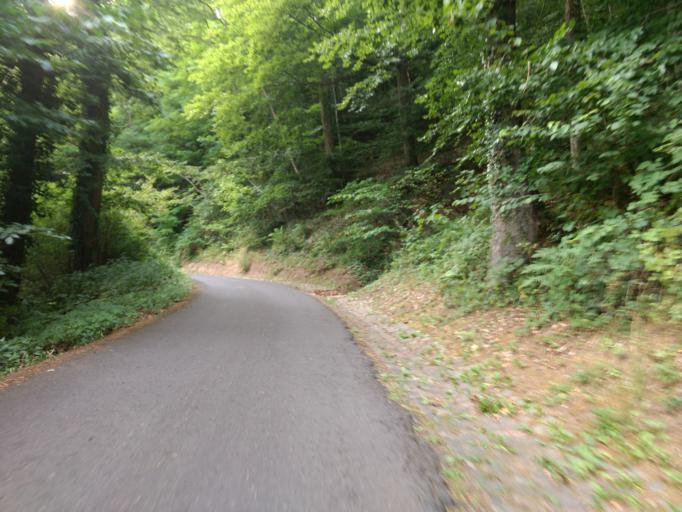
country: DE
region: Saarland
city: Rehlingen-Siersburg
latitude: 49.3390
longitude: 6.6880
